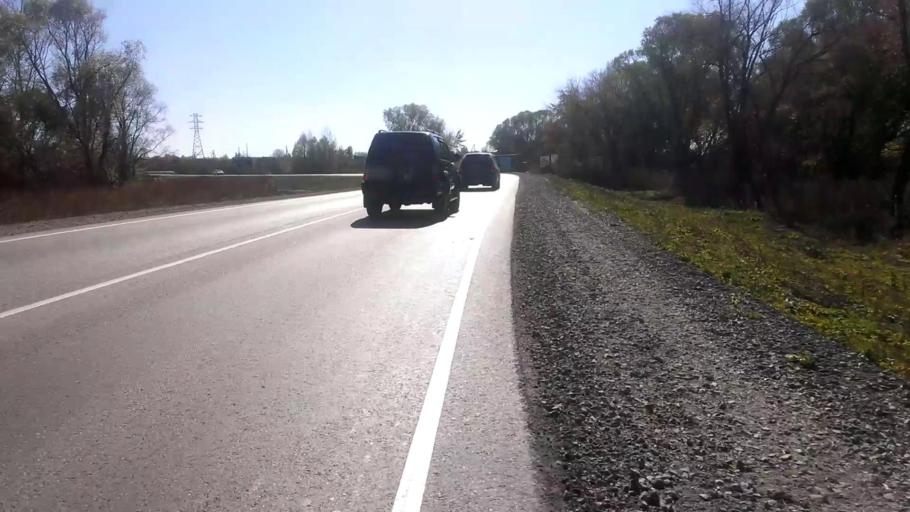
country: RU
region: Altai Krai
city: Sannikovo
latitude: 53.3227
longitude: 83.9428
